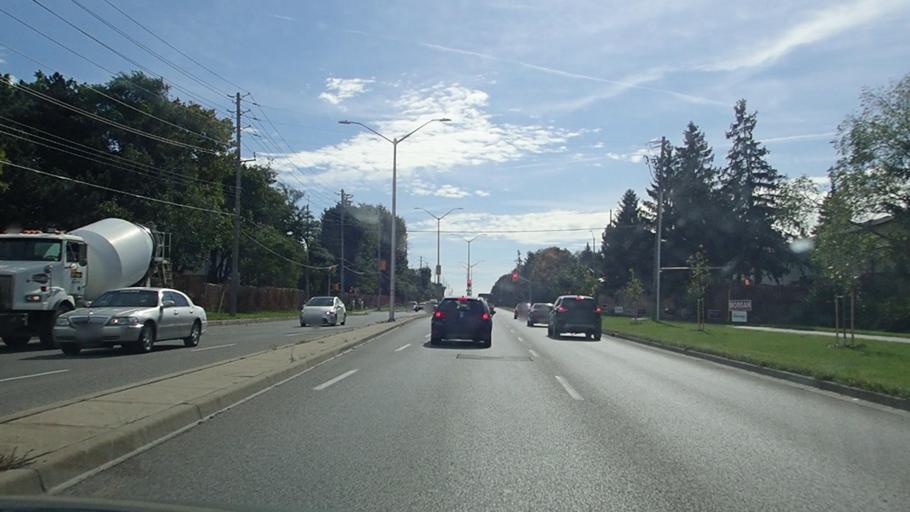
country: CA
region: Ontario
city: London
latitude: 43.0016
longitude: -81.3020
